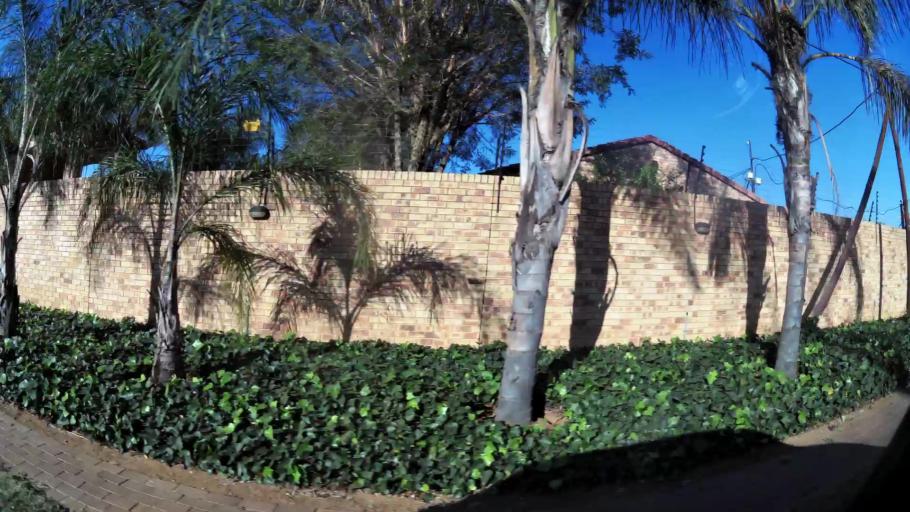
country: ZA
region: Gauteng
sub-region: City of Johannesburg Metropolitan Municipality
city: Roodepoort
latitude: -26.0919
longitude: 27.9461
